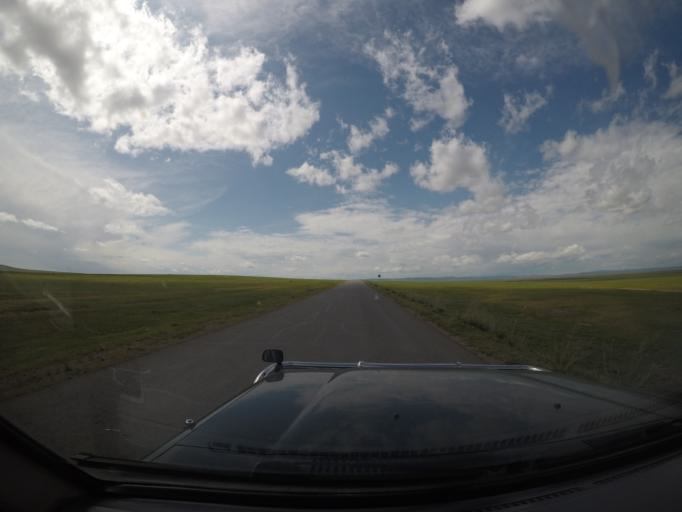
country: MN
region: Hentiy
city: Moron
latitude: 47.4215
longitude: 110.1576
